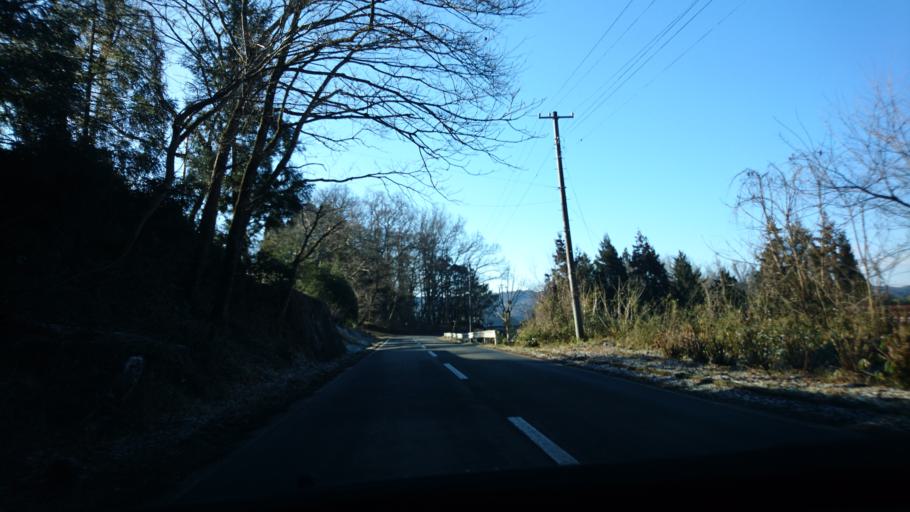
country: JP
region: Iwate
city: Ichinoseki
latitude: 38.8611
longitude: 141.2993
